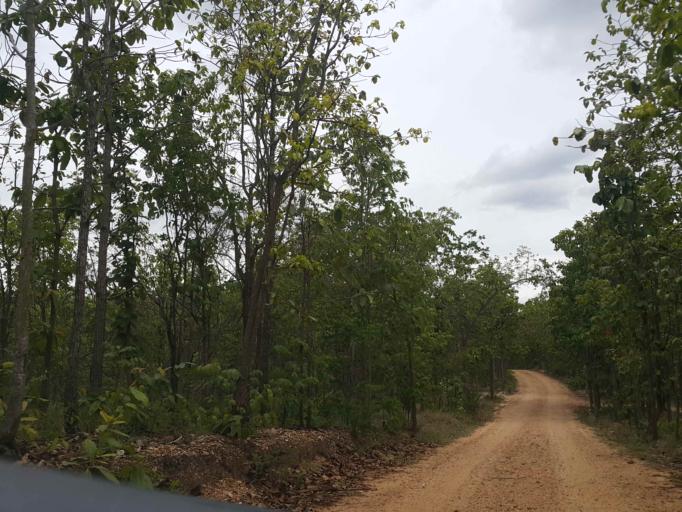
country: TH
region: Chiang Mai
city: Doi Lo
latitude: 18.5025
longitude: 98.7579
